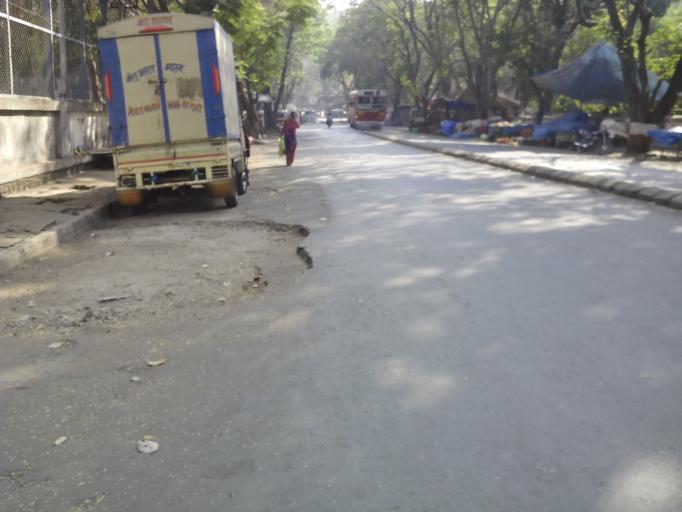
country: IN
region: Maharashtra
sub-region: Mumbai Suburban
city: Borivli
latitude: 19.2084
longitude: 72.8697
